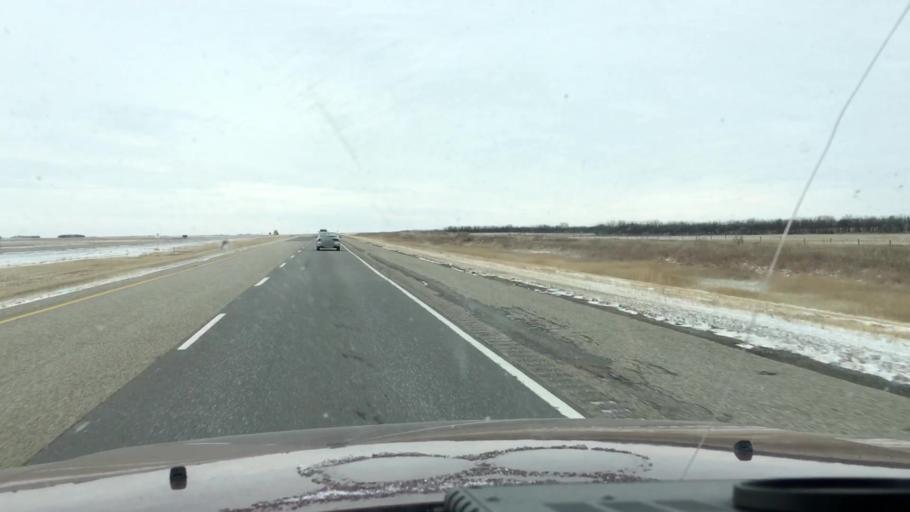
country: CA
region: Saskatchewan
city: Saskatoon
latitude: 51.4693
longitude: -106.2455
